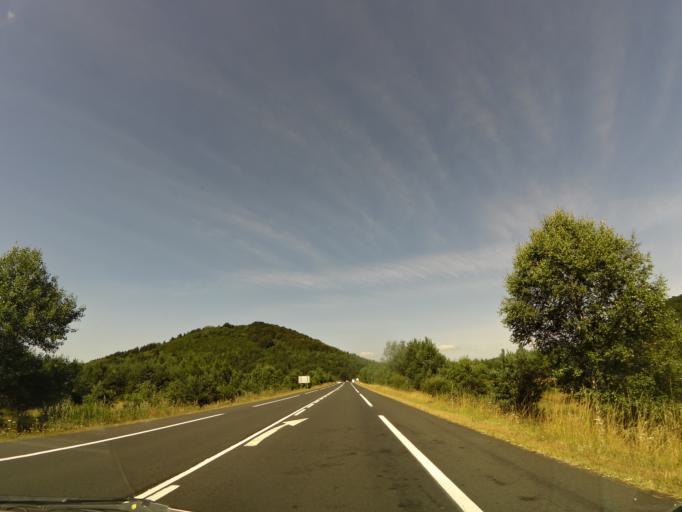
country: FR
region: Auvergne
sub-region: Departement du Puy-de-Dome
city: Aydat
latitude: 45.6833
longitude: 2.9535
